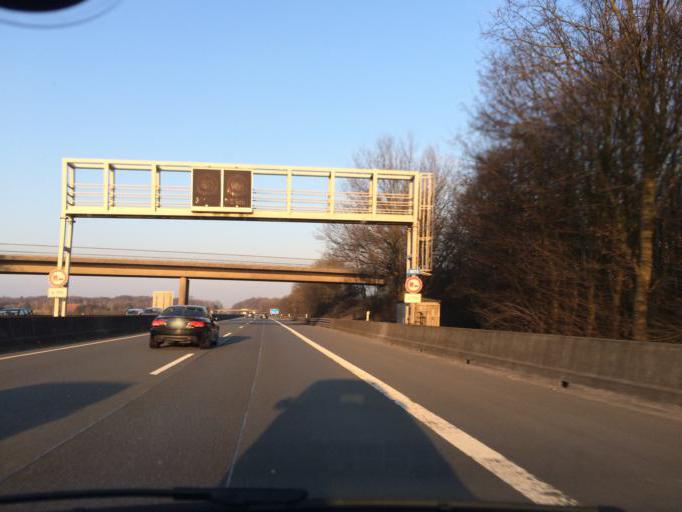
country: DE
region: North Rhine-Westphalia
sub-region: Regierungsbezirk Munster
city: Senden
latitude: 51.9026
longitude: 7.4990
